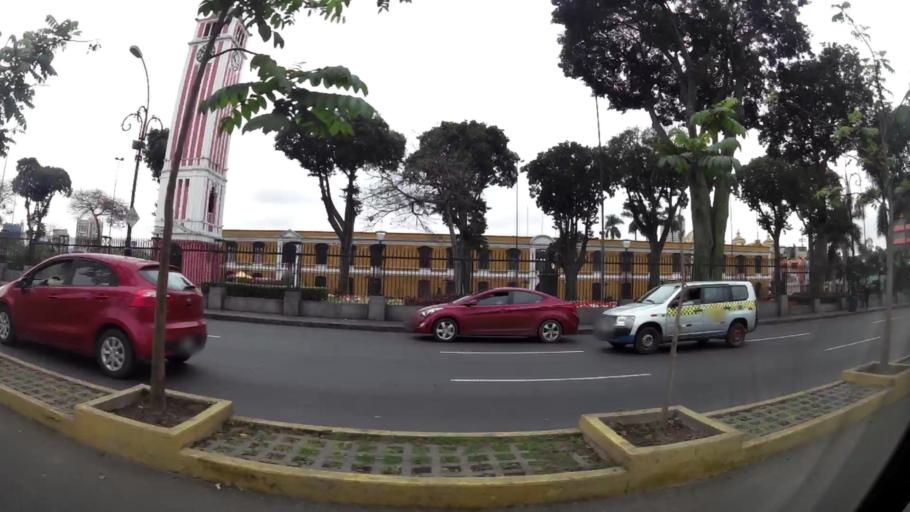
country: PE
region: Lima
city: Lima
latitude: -12.0537
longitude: -77.0315
